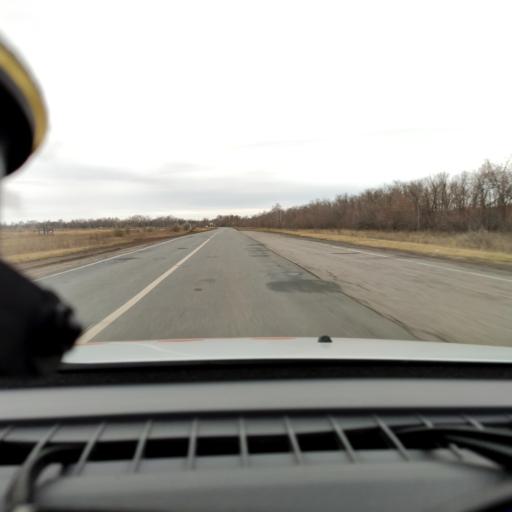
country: RU
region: Samara
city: Smyshlyayevka
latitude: 53.1397
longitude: 50.3815
